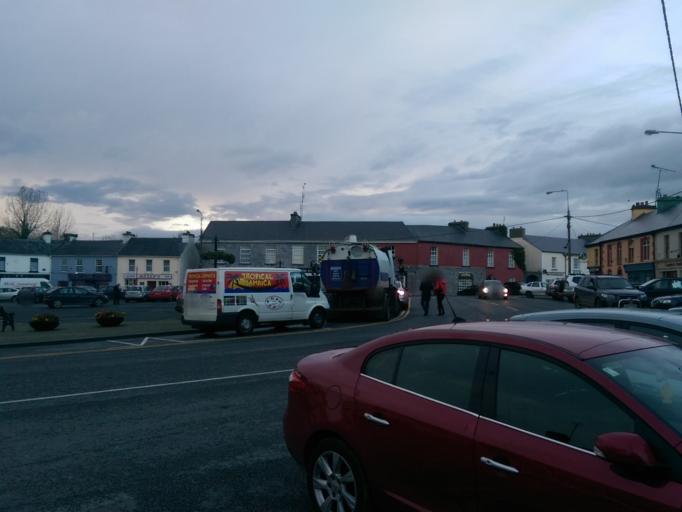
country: IE
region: Connaught
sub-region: County Galway
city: Loughrea
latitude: 53.4699
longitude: -8.5000
